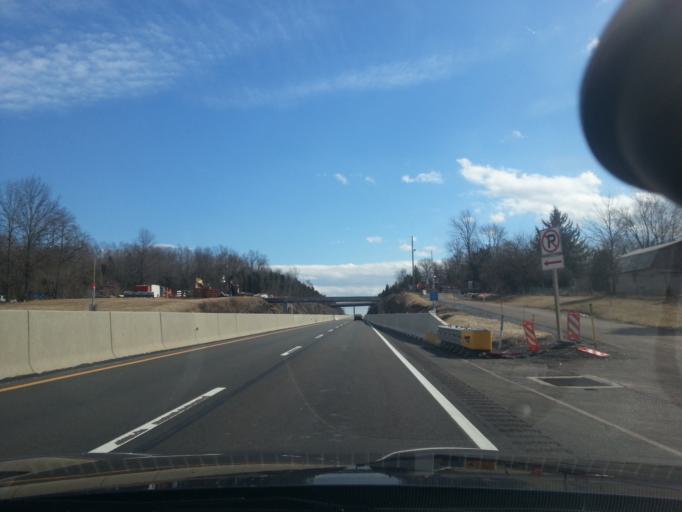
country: US
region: Pennsylvania
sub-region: Montgomery County
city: Woxall
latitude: 40.3545
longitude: -75.3930
